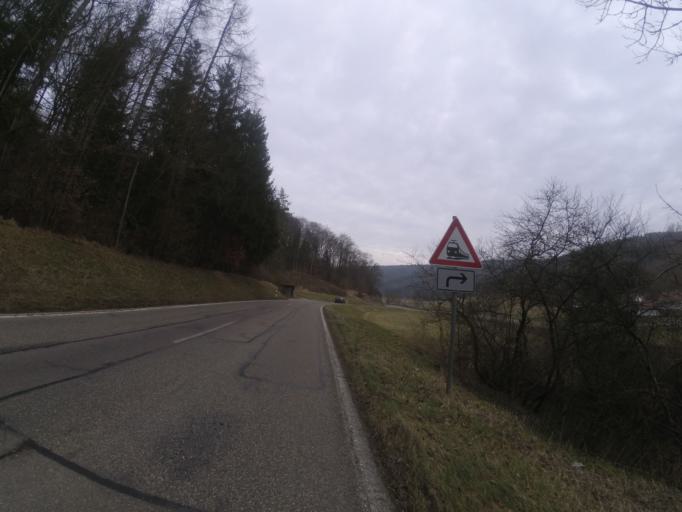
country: DE
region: Baden-Wuerttemberg
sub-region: Tuebingen Region
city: Schelklingen
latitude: 48.3681
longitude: 9.6558
